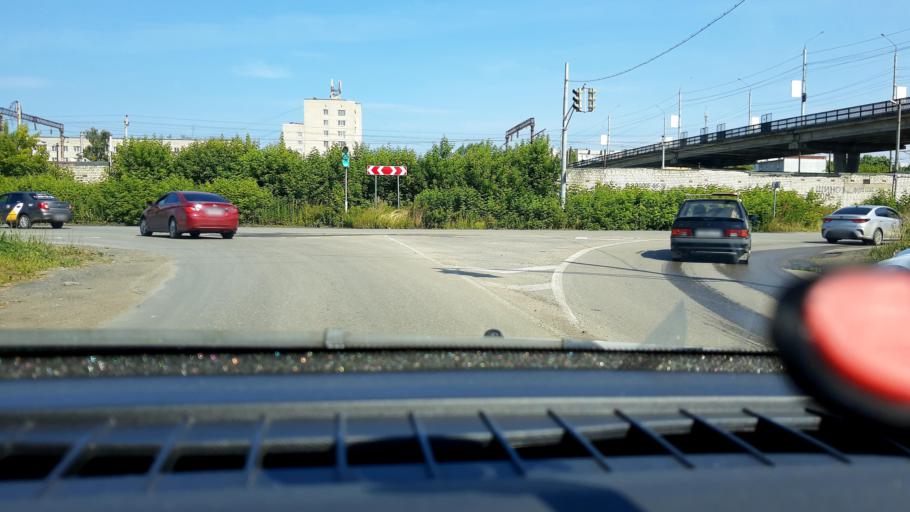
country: RU
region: Nizjnij Novgorod
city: Dzerzhinsk
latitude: 56.2339
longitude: 43.4888
